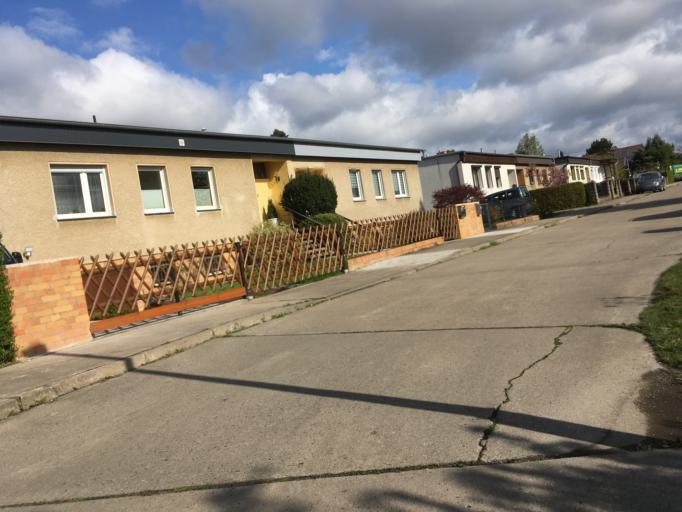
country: DE
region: Berlin
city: Friedrichsfelde
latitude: 52.5148
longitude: 13.5295
